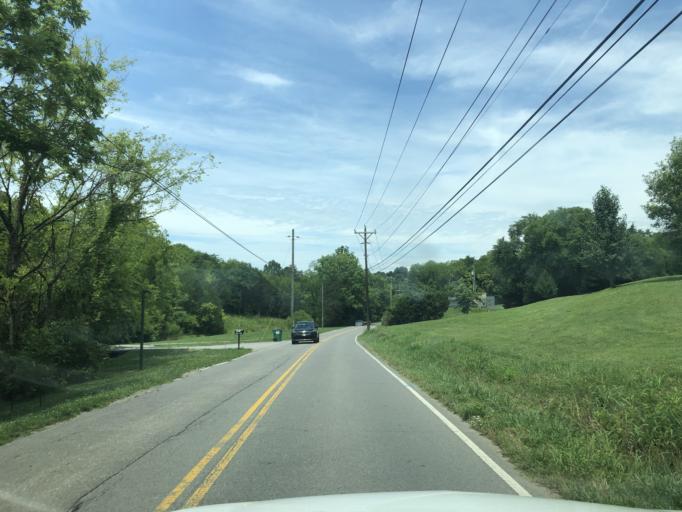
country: US
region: Tennessee
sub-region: Rutherford County
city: La Vergne
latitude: 36.0306
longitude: -86.6519
